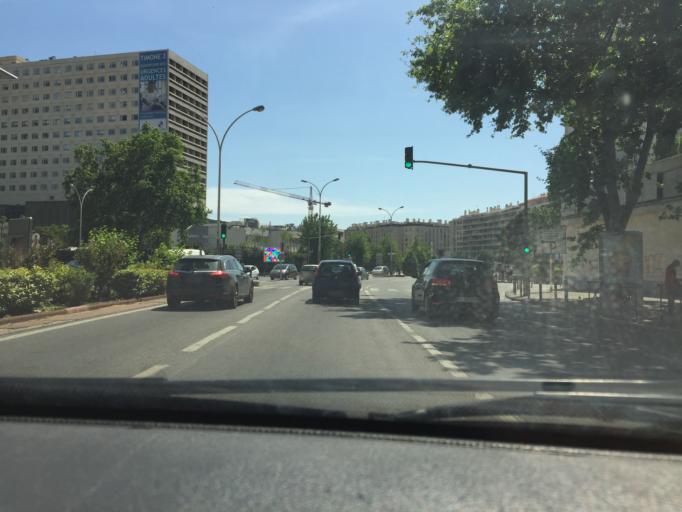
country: FR
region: Provence-Alpes-Cote d'Azur
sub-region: Departement des Bouches-du-Rhone
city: Marseille 05
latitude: 43.2929
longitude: 5.4013
